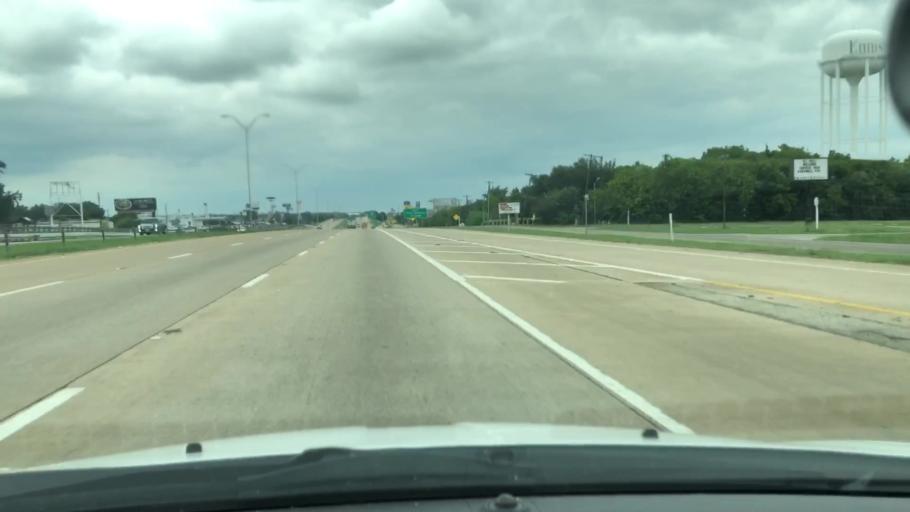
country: US
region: Texas
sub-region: Ellis County
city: Ennis
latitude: 32.3272
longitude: -96.6105
